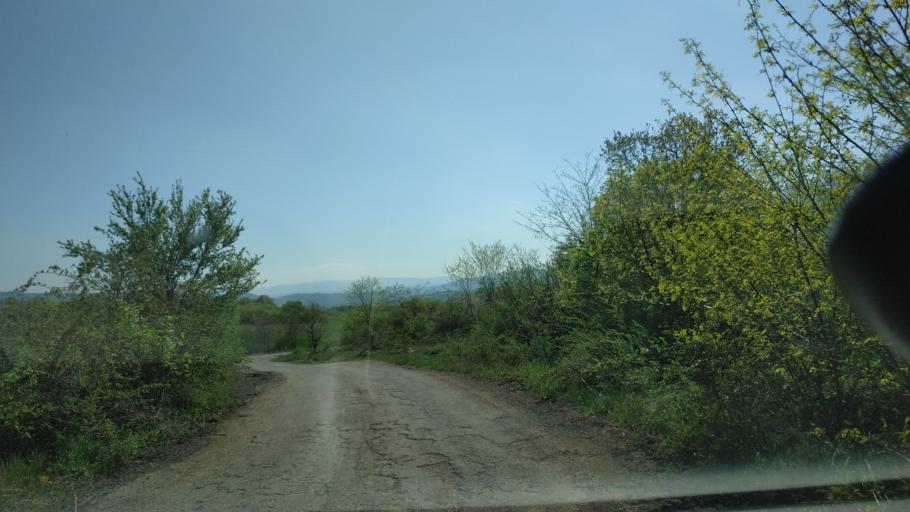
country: RS
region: Central Serbia
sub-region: Zajecarski Okrug
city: Soko Banja
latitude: 43.4976
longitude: 21.8811
